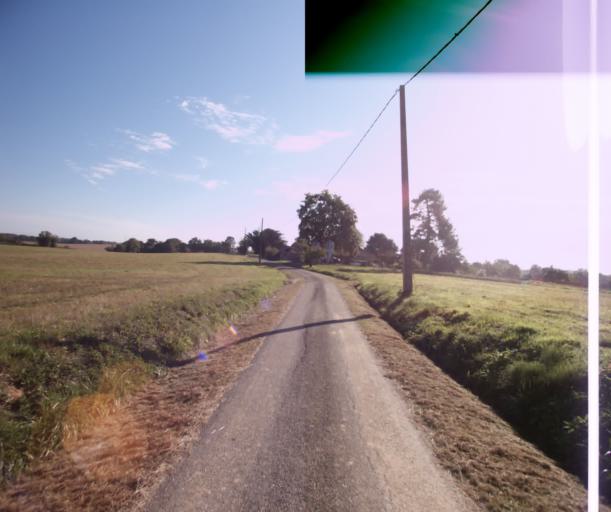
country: FR
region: Midi-Pyrenees
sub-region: Departement du Gers
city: Cazaubon
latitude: 43.9157
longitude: -0.0064
